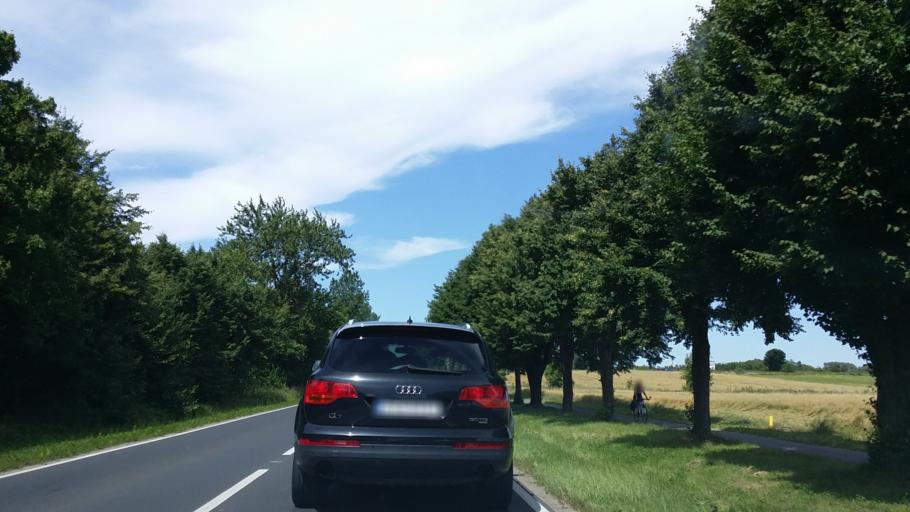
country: PL
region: West Pomeranian Voivodeship
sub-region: Powiat koszalinski
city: Mielno
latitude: 54.2437
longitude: 16.0662
